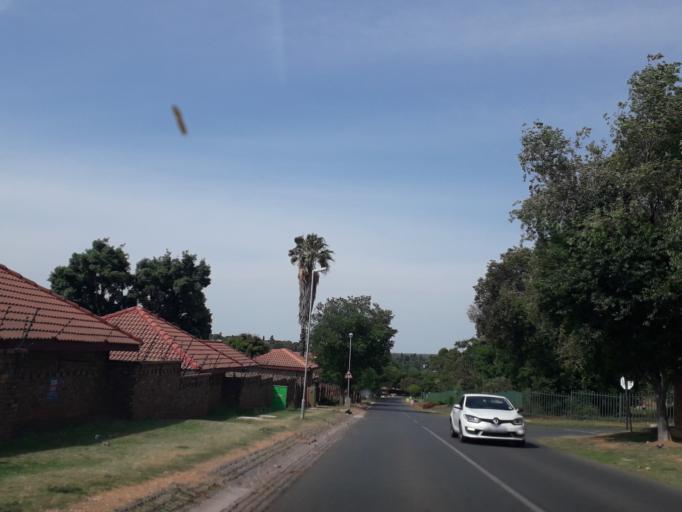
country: ZA
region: Gauteng
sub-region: City of Johannesburg Metropolitan Municipality
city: Roodepoort
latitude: -26.0733
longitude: 27.9569
